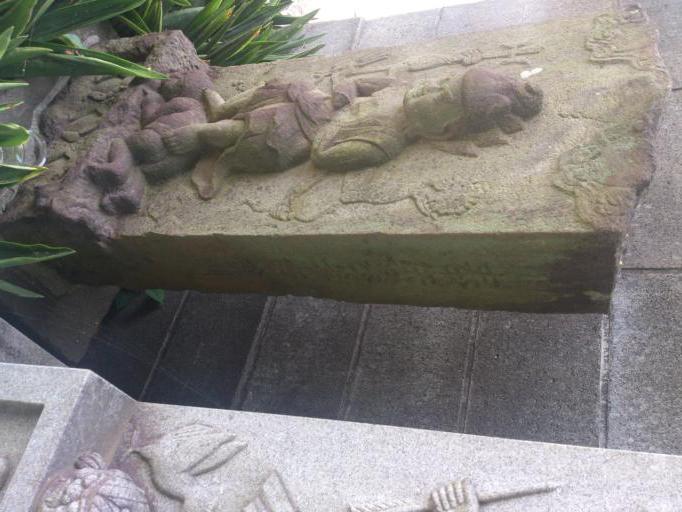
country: JP
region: Chiba
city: Matsudo
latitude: 35.8006
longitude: 139.9329
